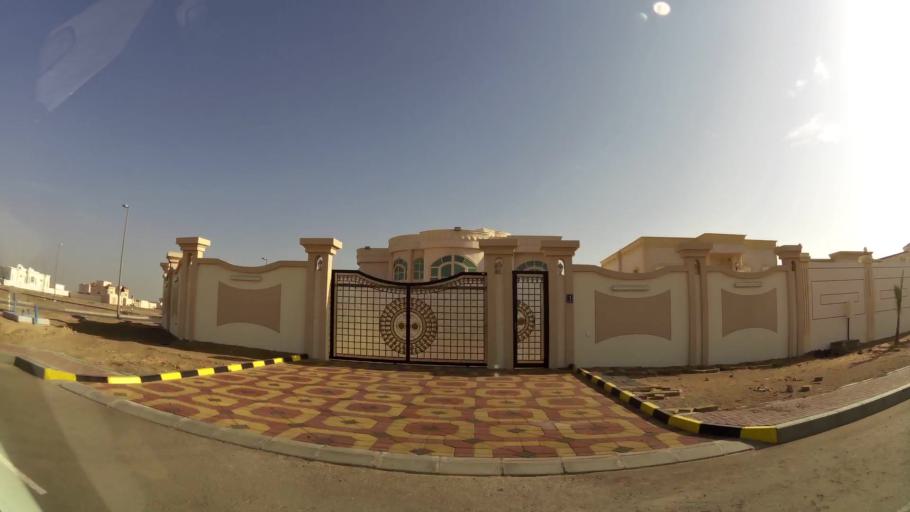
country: AE
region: Abu Dhabi
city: Al Ain
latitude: 24.0516
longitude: 55.8451
